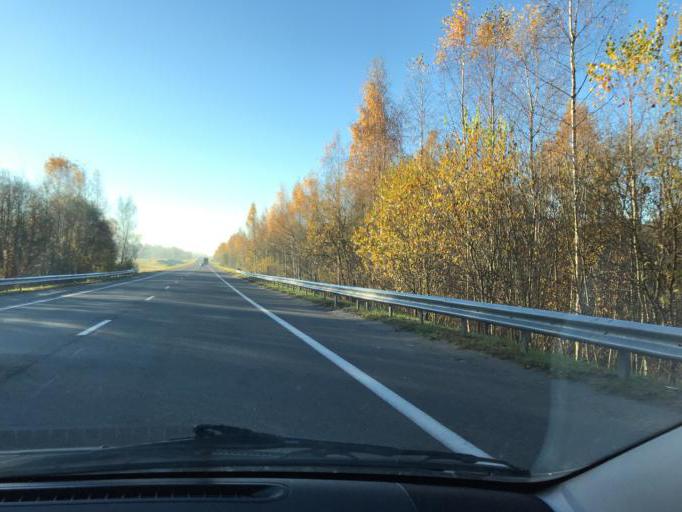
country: BY
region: Vitebsk
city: Vitebsk
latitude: 55.0096
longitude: 30.3322
